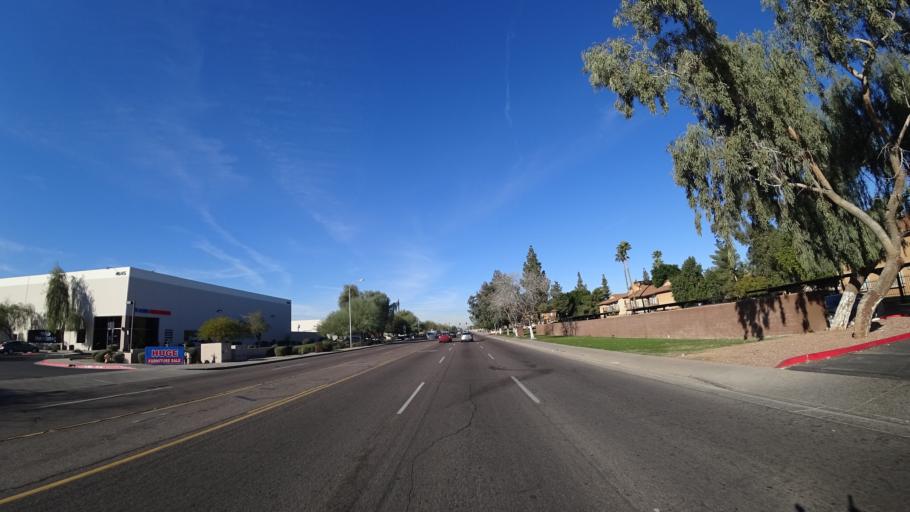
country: US
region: Arizona
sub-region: Maricopa County
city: Glendale
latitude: 33.4660
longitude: -112.1574
